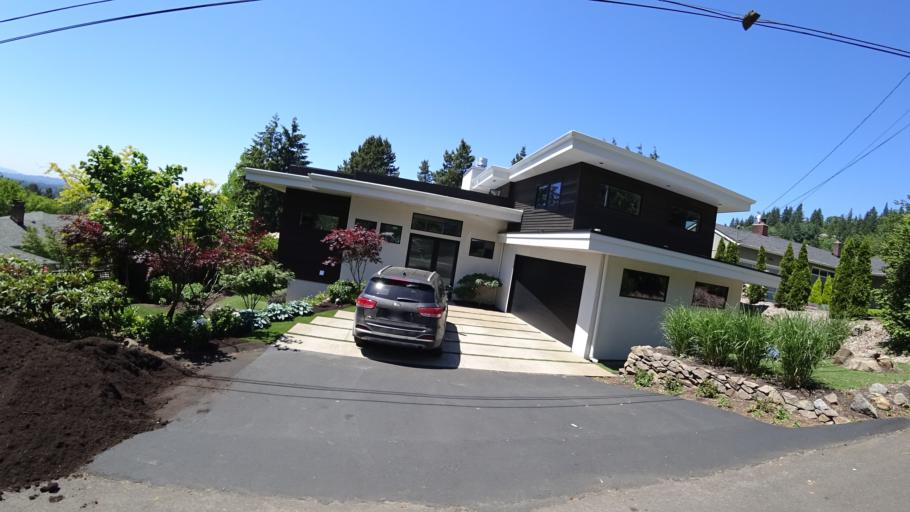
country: US
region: Oregon
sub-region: Washington County
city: West Slope
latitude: 45.4964
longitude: -122.7163
